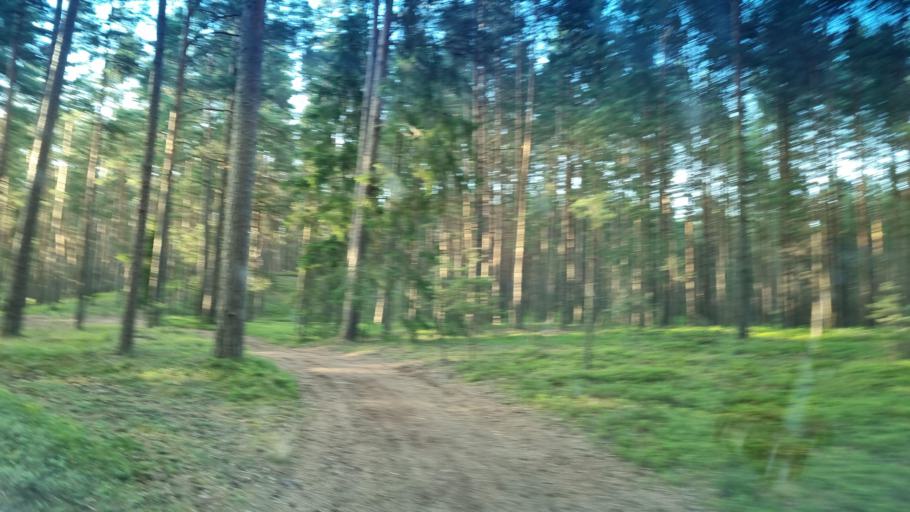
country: LV
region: Kuldigas Rajons
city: Kuldiga
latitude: 57.1925
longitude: 22.1832
